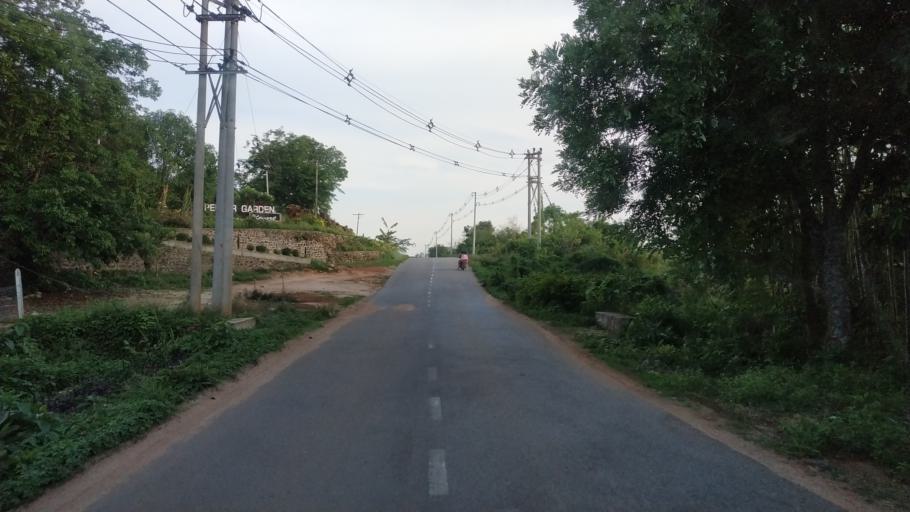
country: MM
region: Mon
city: Kyaikto
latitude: 17.4119
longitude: 97.0726
